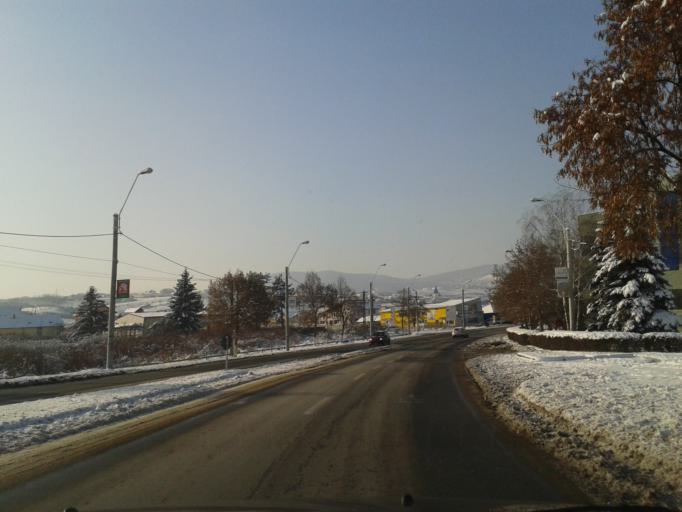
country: RO
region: Hunedoara
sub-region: Municipiul Deva
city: Deva
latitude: 45.8599
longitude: 22.9236
